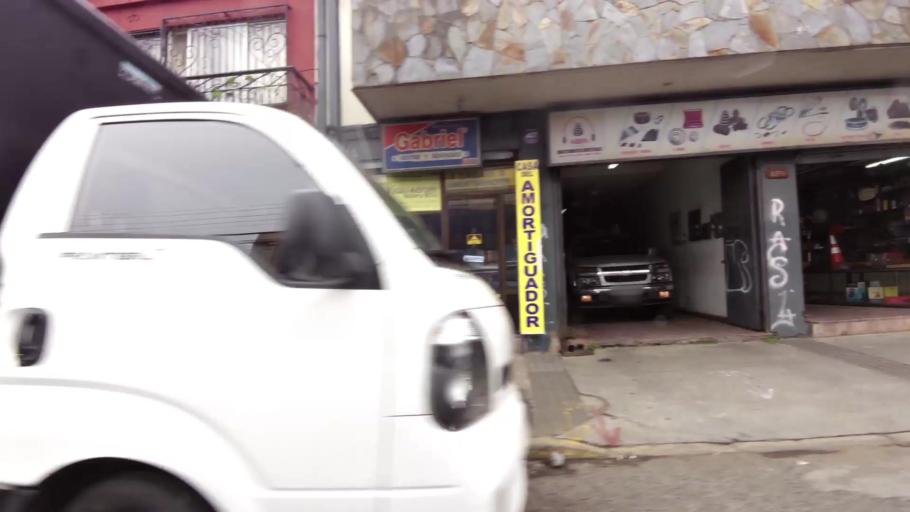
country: CL
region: Biobio
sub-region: Provincia de Concepcion
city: Concepcion
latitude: -36.8275
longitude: -73.0590
